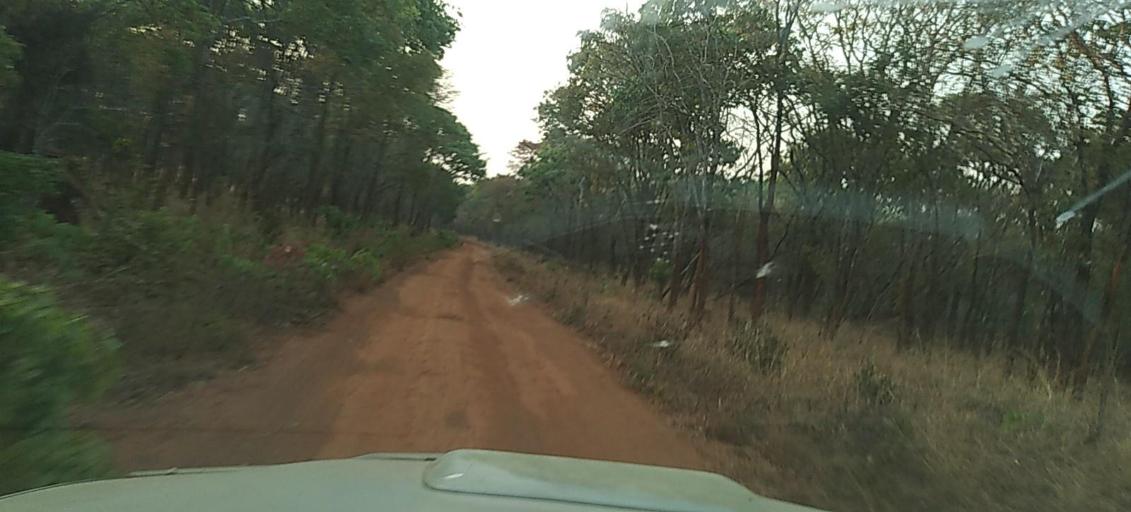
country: ZM
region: North-Western
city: Kasempa
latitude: -13.0833
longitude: 26.3956
